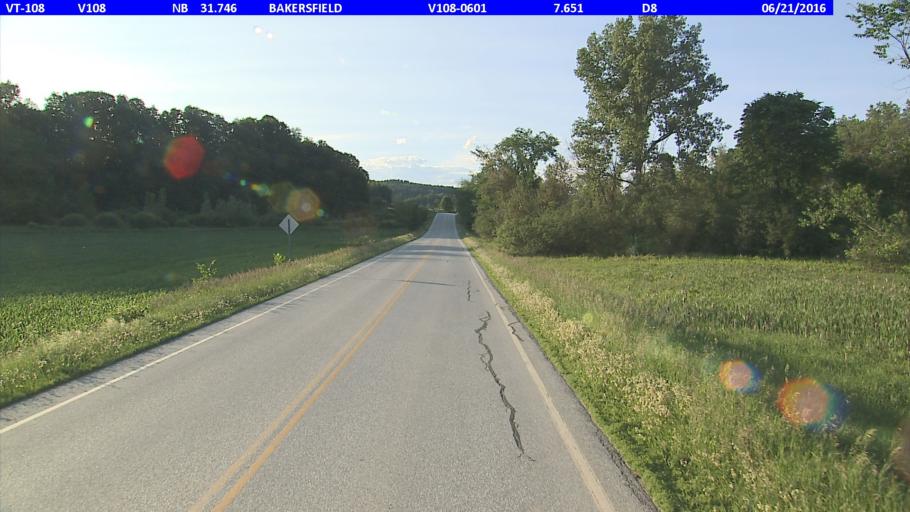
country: US
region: Vermont
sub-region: Franklin County
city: Enosburg Falls
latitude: 44.8331
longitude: -72.8033
